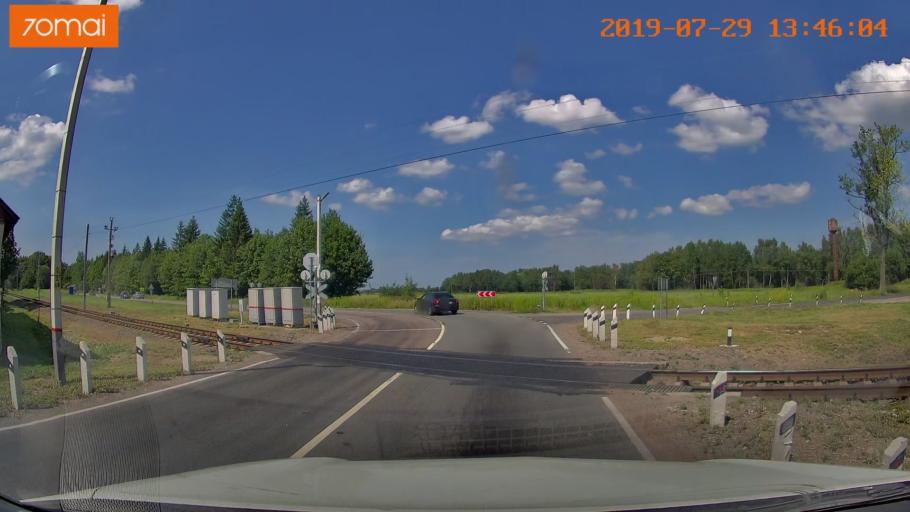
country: RU
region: Kaliningrad
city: Primorsk
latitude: 54.7400
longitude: 20.0690
